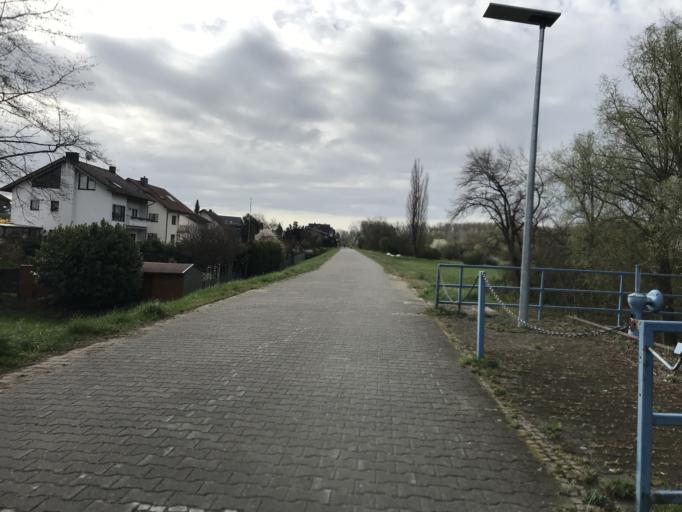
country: DE
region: Hesse
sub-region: Regierungsbezirk Darmstadt
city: Ginsheim-Gustavsburg
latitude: 49.9706
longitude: 8.3345
